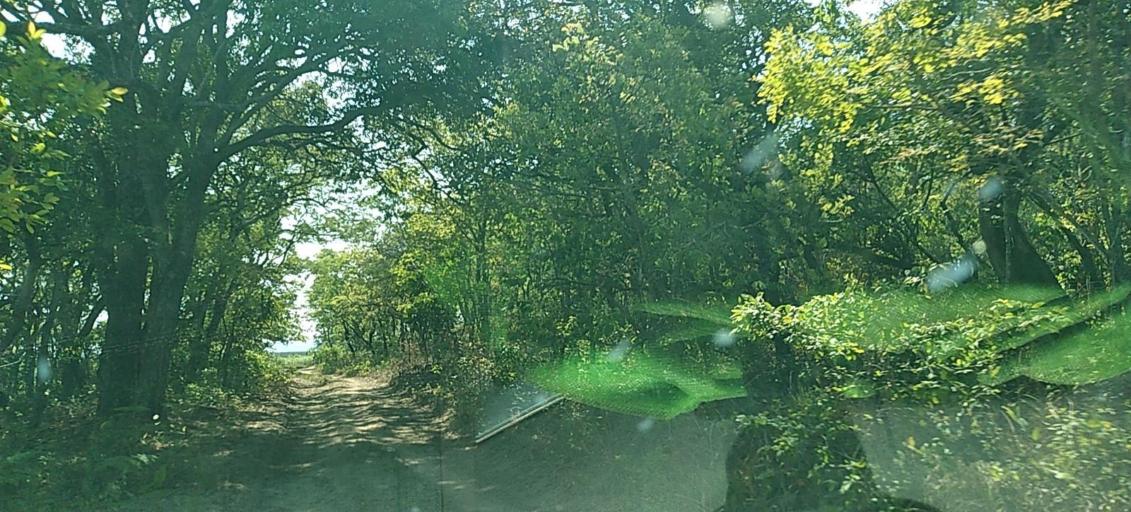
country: ZM
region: North-Western
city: Mwinilunga
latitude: -11.2733
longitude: 24.9862
